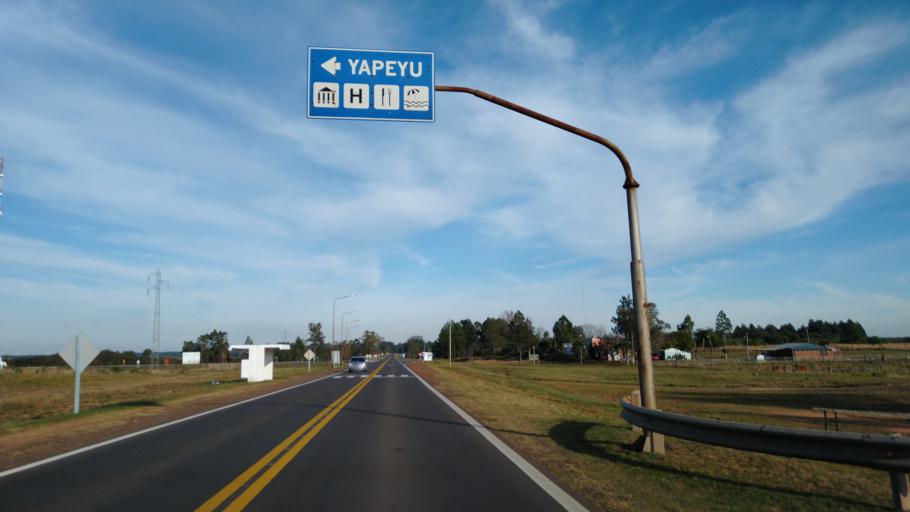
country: AR
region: Corrientes
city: Yapeyu
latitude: -29.4218
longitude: -56.8435
